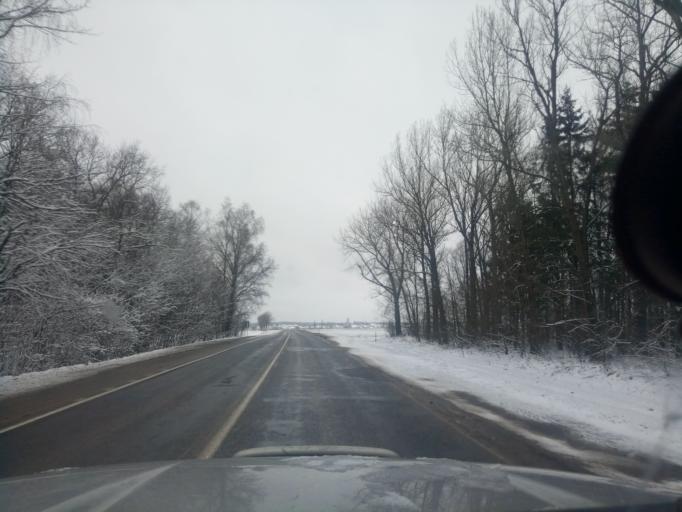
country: BY
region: Minsk
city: Kapyl'
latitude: 53.1293
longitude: 27.0807
